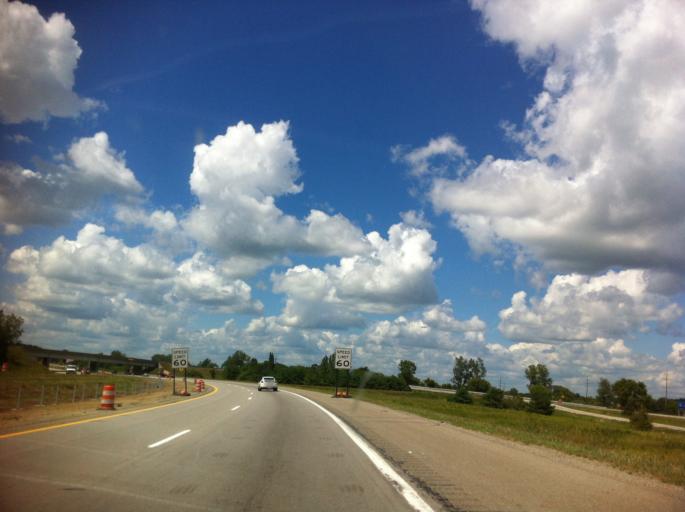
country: US
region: Michigan
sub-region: Washtenaw County
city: Milan
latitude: 42.0982
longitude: -83.6747
